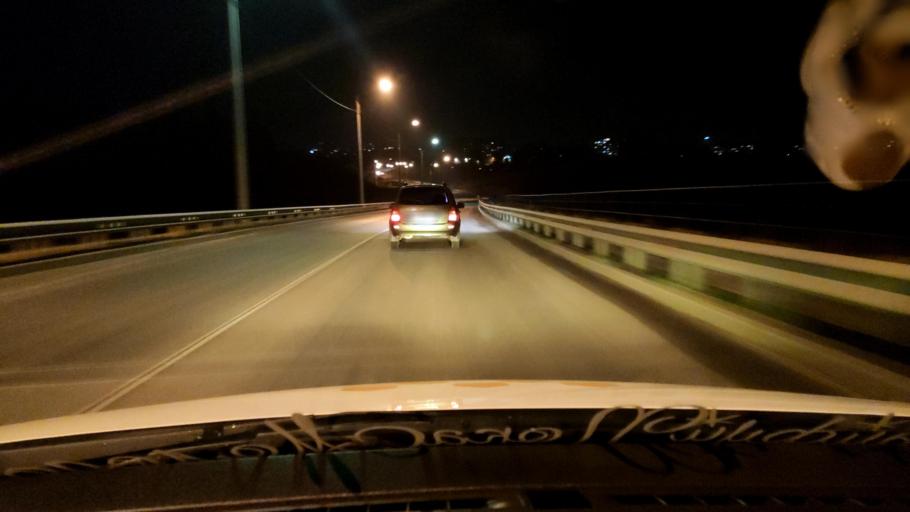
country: RU
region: Voronezj
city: Semiluki
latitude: 51.6717
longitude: 39.0352
